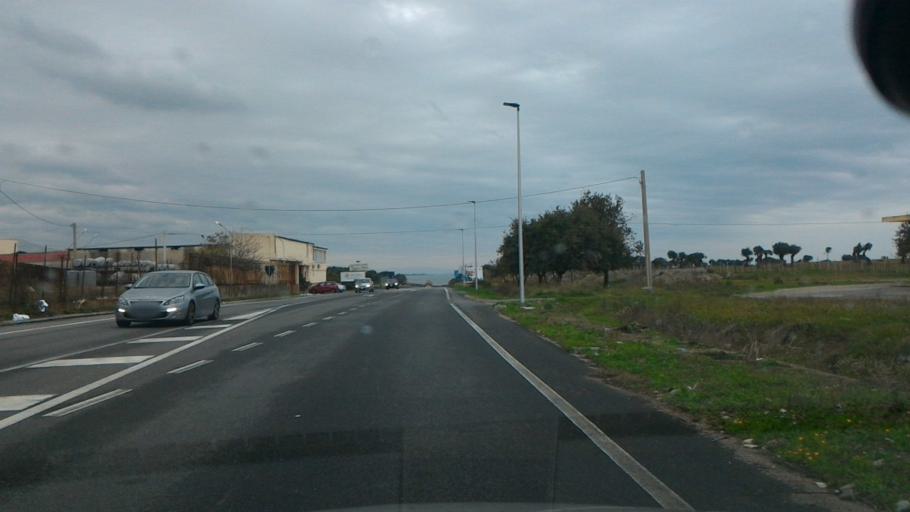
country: IT
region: Calabria
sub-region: Provincia di Crotone
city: Ciro Marina
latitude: 39.4006
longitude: 17.1153
